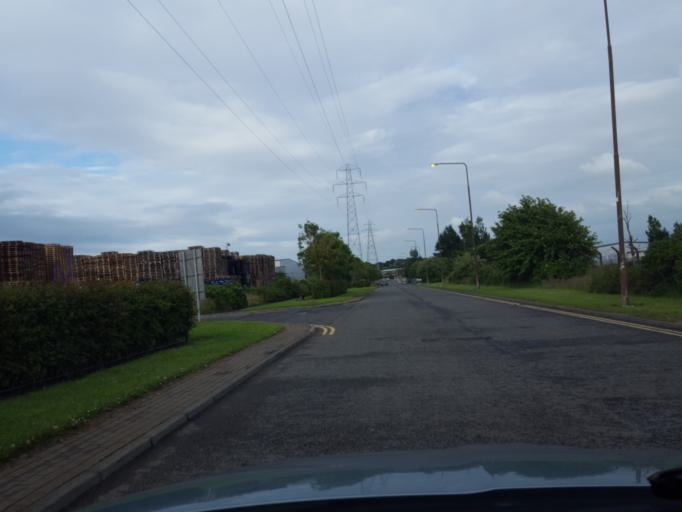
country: GB
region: Scotland
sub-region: West Lothian
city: Blackburn
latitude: 55.8845
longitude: -3.6328
